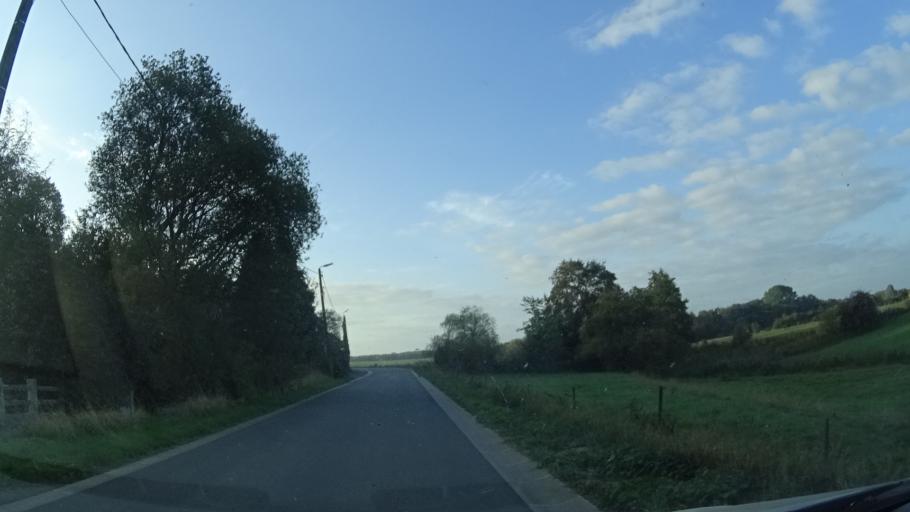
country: BE
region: Wallonia
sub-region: Province de Namur
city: Cerfontaine
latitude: 50.2105
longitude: 4.3593
